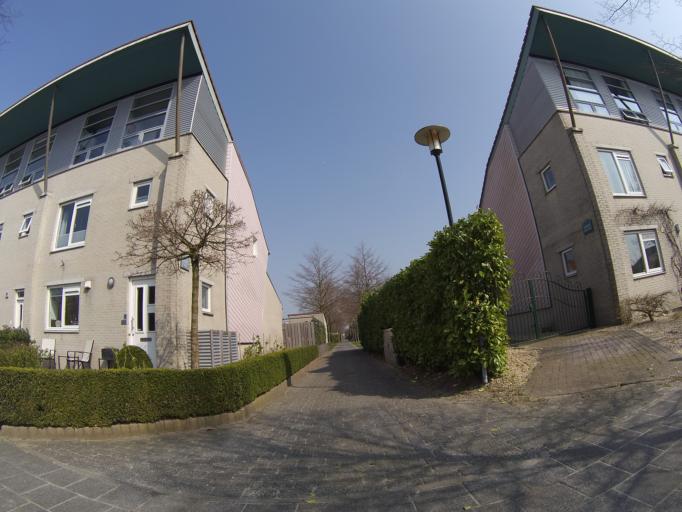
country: NL
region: Utrecht
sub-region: Gemeente Amersfoort
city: Hoogland
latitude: 52.1897
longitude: 5.4014
